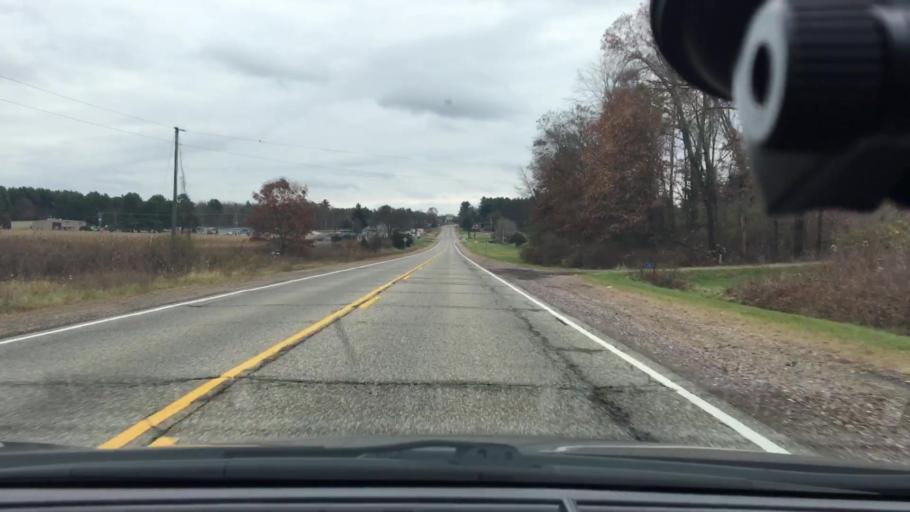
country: US
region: Wisconsin
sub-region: Columbia County
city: Wisconsin Dells
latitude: 43.6375
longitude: -89.7958
